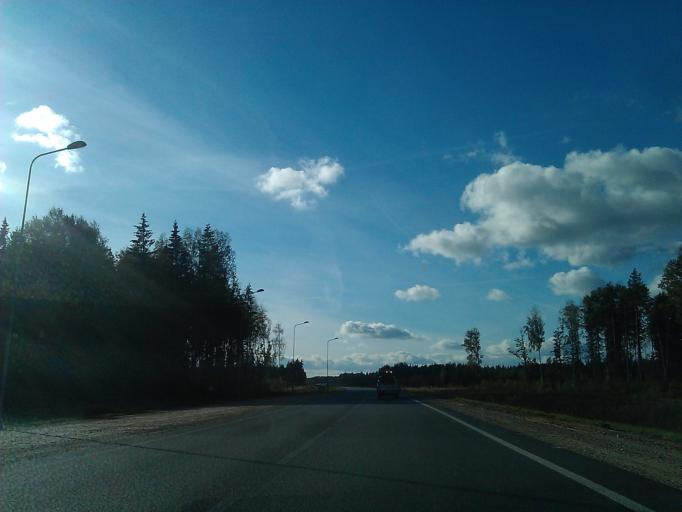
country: LV
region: Koknese
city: Koknese
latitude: 56.6670
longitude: 25.4547
